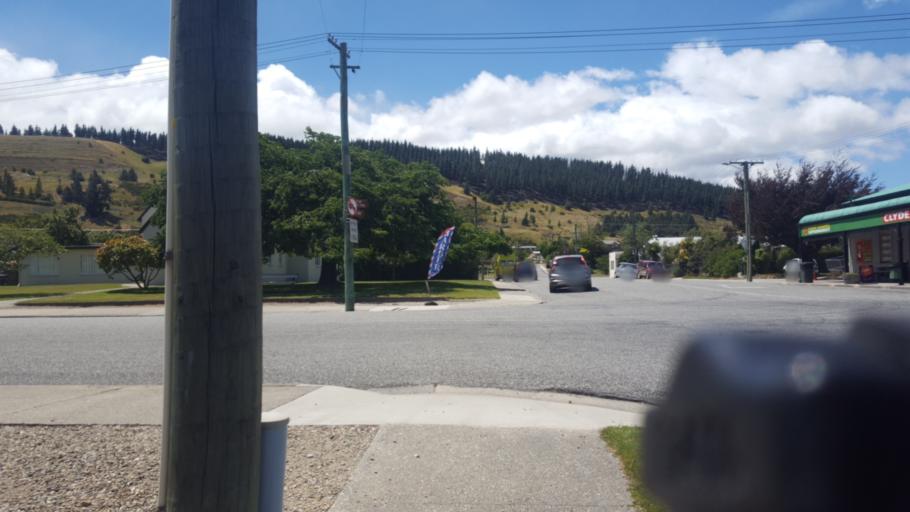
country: NZ
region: Otago
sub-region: Queenstown-Lakes District
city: Wanaka
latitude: -45.1888
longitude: 169.3187
